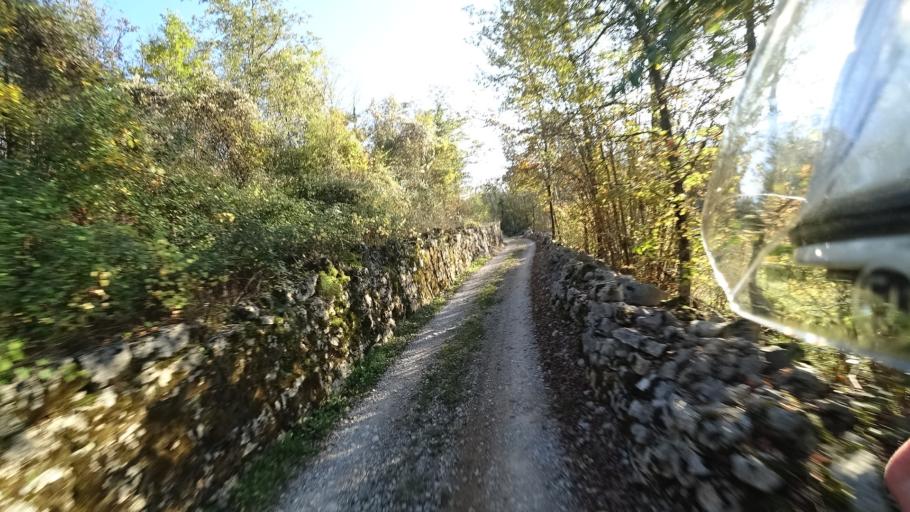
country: HR
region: Primorsko-Goranska
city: Matulji
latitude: 45.4013
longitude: 14.2972
